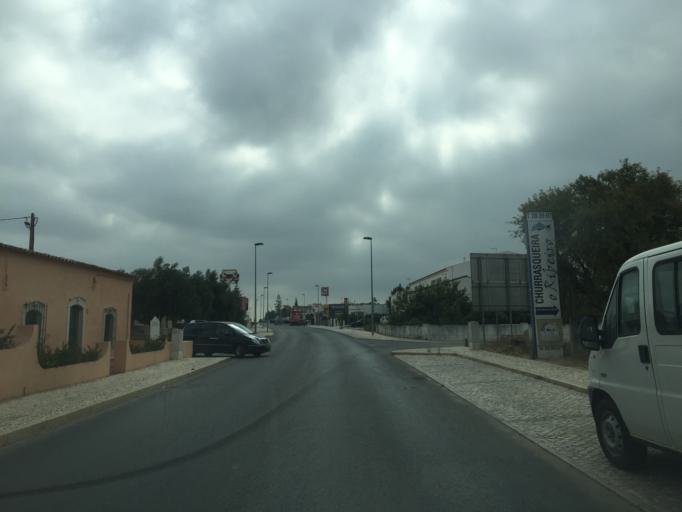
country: PT
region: Faro
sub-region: Loule
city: Almancil
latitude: 37.0845
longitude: -8.0235
